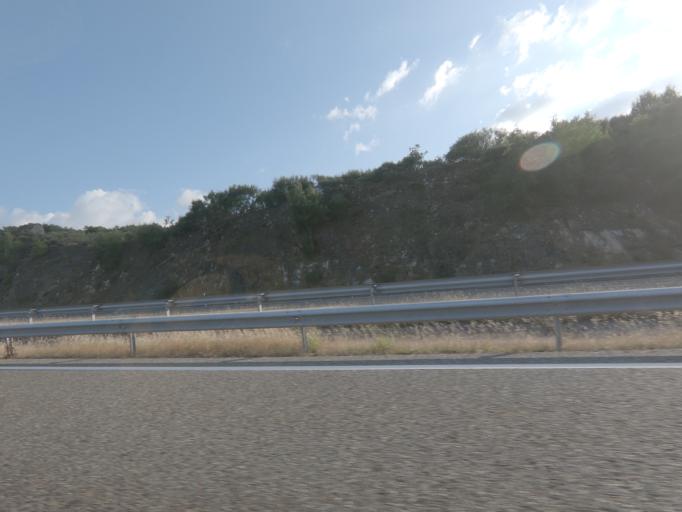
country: ES
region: Galicia
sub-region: Provincia de Ourense
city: Cualedro
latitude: 42.0076
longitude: -7.5676
